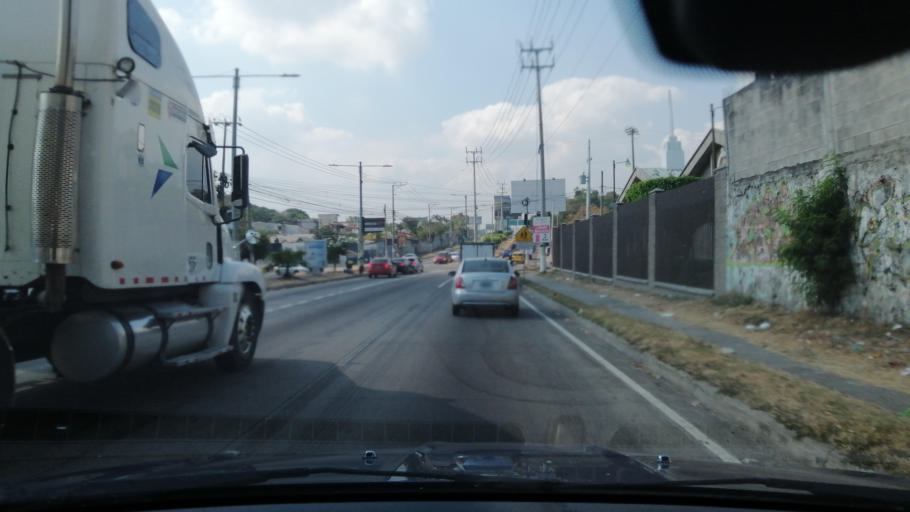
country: SV
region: San Salvador
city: Mejicanos
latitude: 13.7403
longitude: -89.2174
